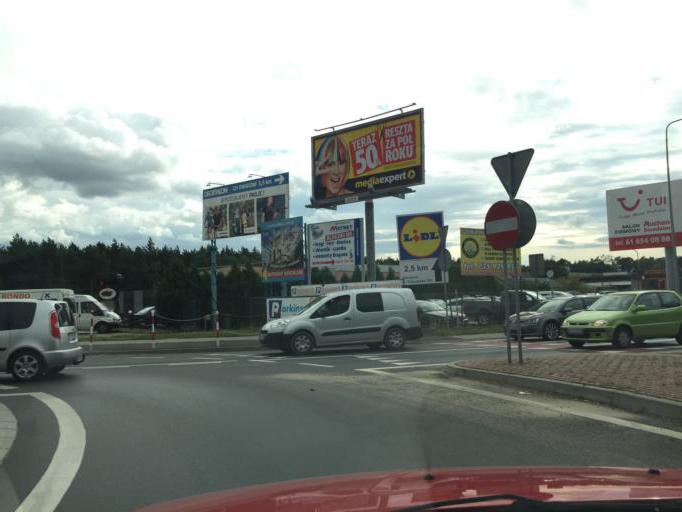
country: PL
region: Greater Poland Voivodeship
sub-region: Powiat poznanski
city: Baranowo
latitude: 52.4149
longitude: 16.7902
